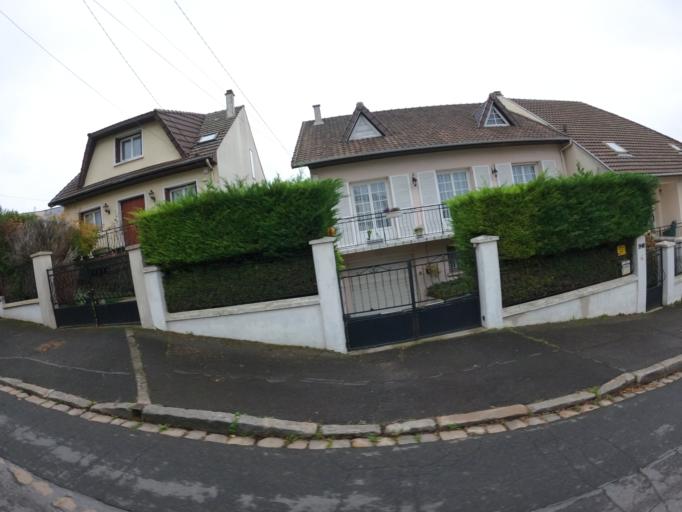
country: FR
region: Ile-de-France
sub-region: Departement du Val-de-Marne
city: Sucy-en-Brie
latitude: 48.7791
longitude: 2.5217
